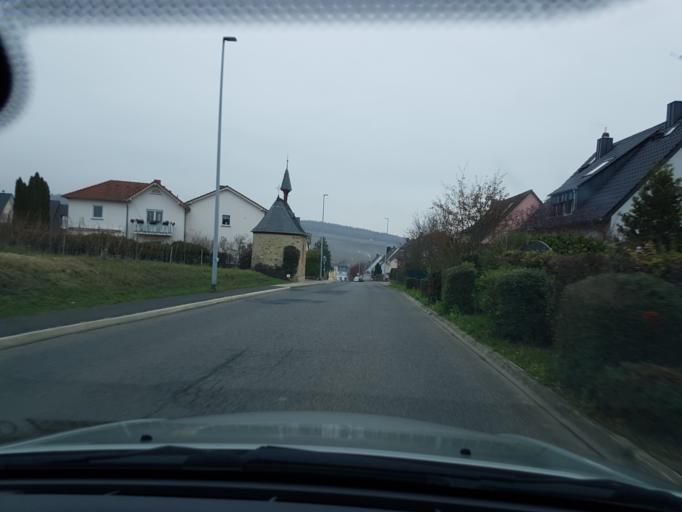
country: DE
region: Hesse
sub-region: Regierungsbezirk Darmstadt
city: Kiedrich
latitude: 50.0385
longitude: 8.0763
